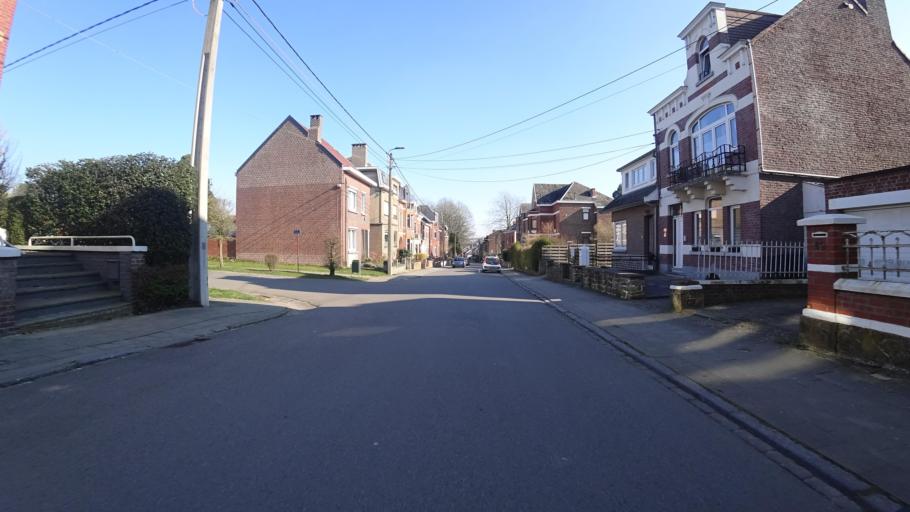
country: BE
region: Wallonia
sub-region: Province de Namur
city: Gembloux
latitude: 50.5618
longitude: 4.6855
